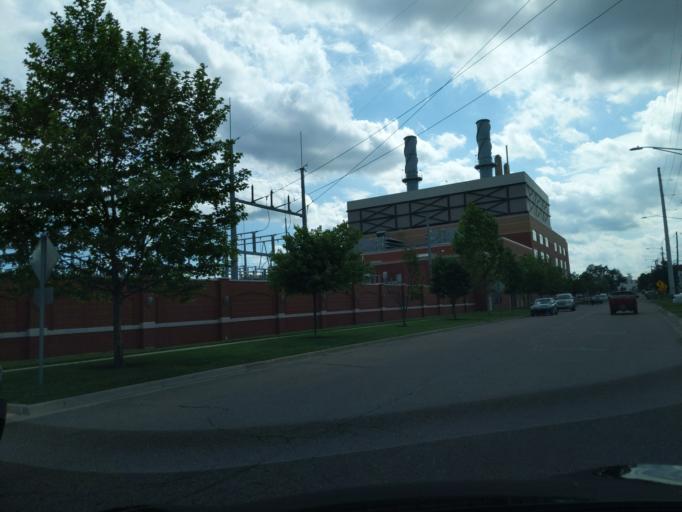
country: US
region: Michigan
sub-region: Ingham County
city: Lansing
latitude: 42.7202
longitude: -84.5493
